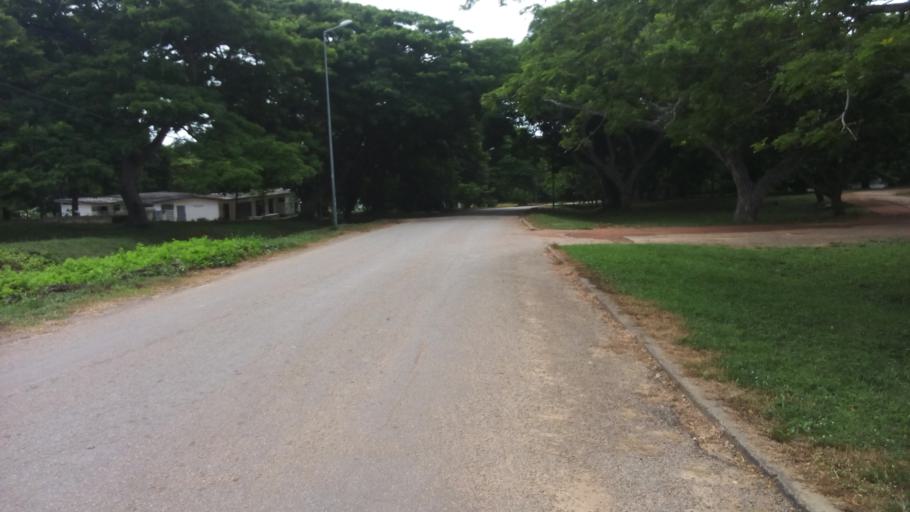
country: GH
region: Central
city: Cape Coast
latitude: 5.1269
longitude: -1.2913
